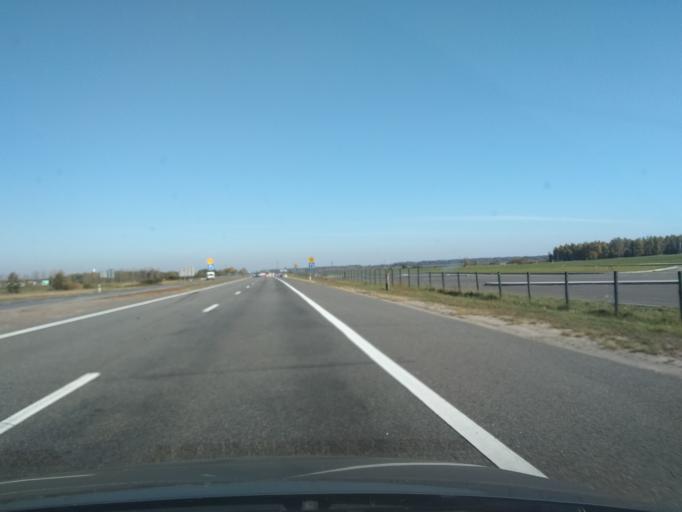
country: BY
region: Brest
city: Byaroza
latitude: 52.4970
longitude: 24.9849
